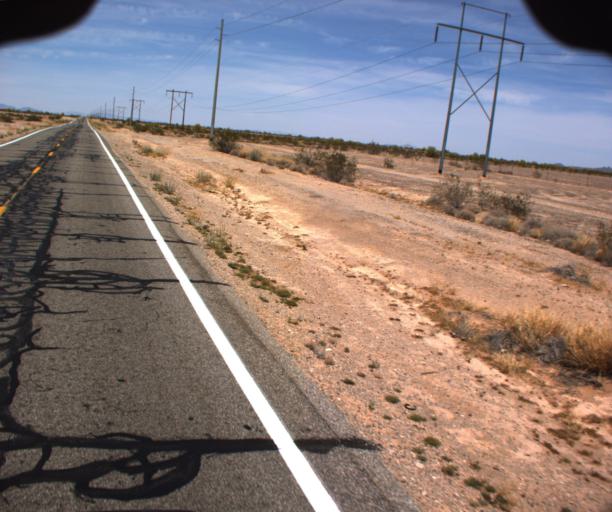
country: US
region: Arizona
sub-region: La Paz County
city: Quartzsite
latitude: 33.8202
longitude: -114.2170
